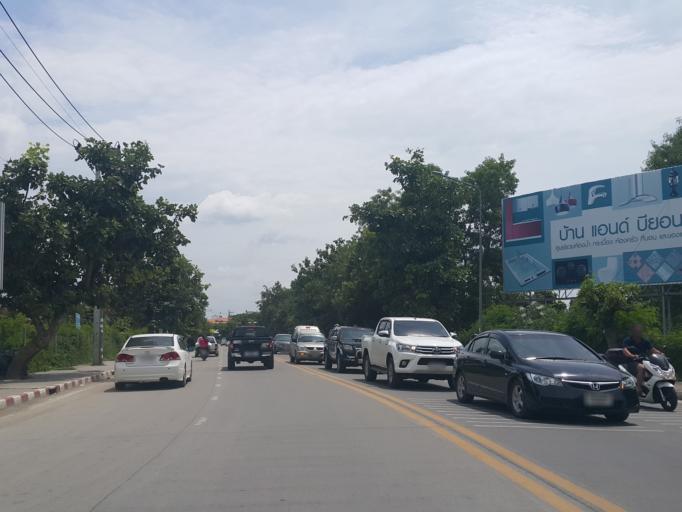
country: TH
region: Chiang Mai
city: Chiang Mai
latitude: 18.8038
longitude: 98.9948
